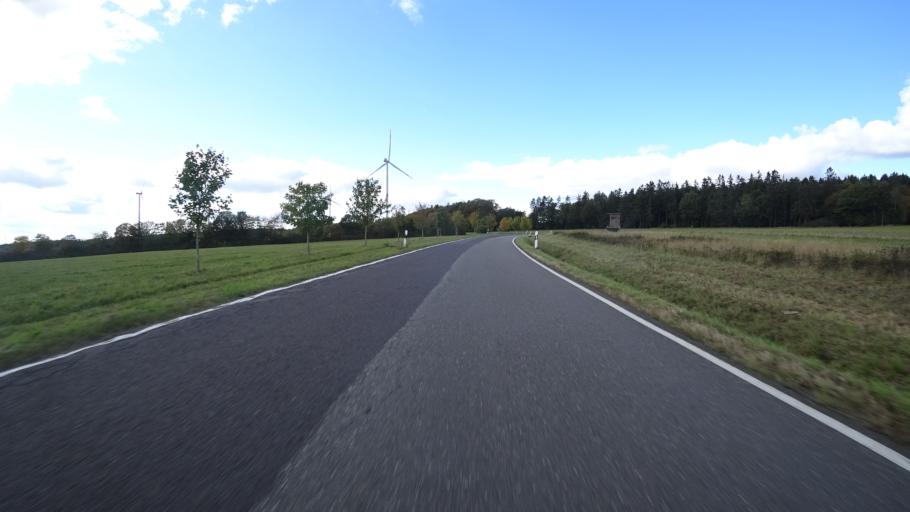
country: DE
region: Rheinland-Pfalz
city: Liebshausen
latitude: 50.0389
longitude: 7.6266
